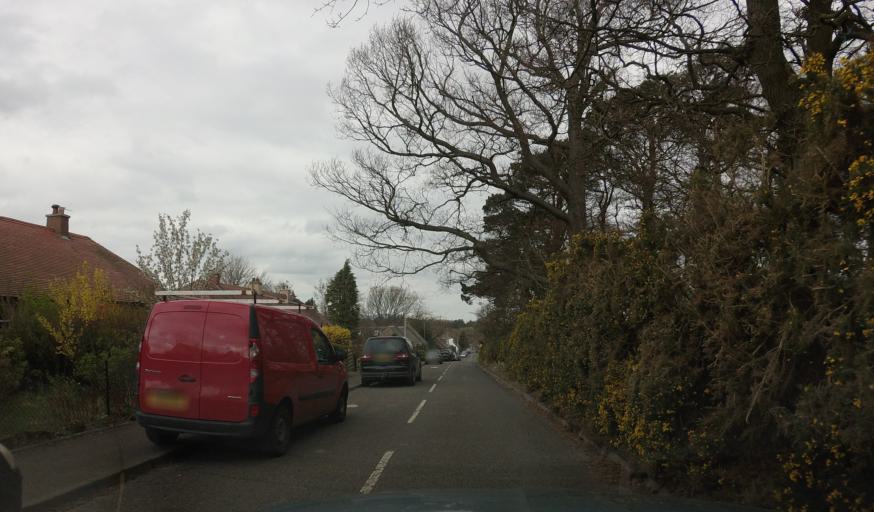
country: GB
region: Scotland
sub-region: Midlothian
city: Gorebridge
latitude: 55.8131
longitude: -3.0886
